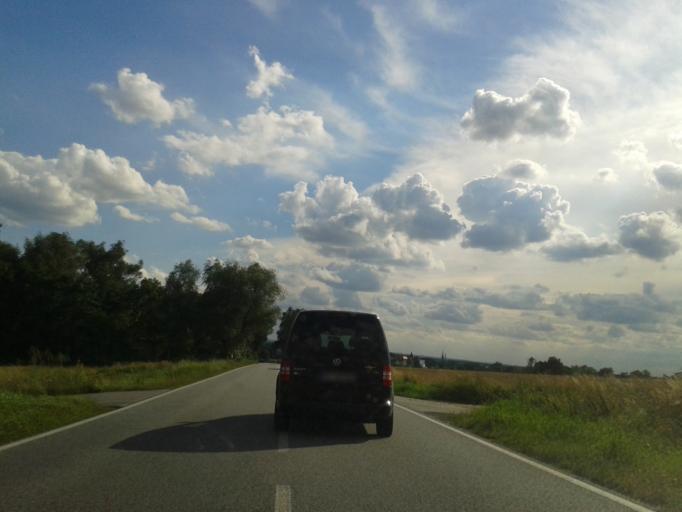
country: DE
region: Saxony
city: Radeberg
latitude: 51.1312
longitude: 13.9412
